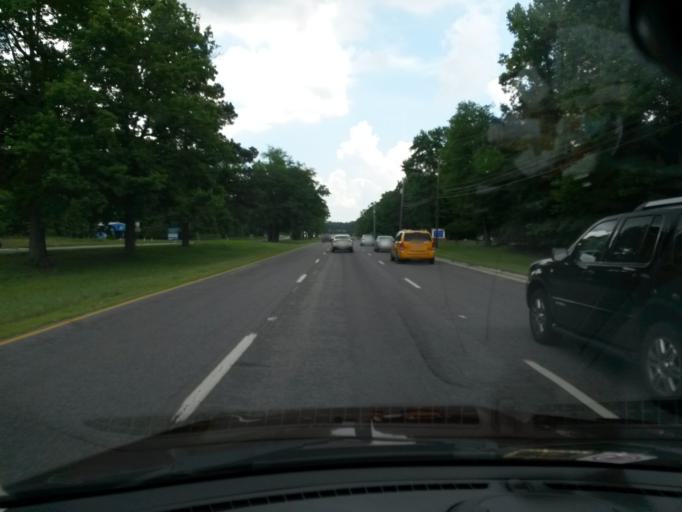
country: US
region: Virginia
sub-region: Chesterfield County
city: Enon
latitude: 37.3470
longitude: -77.3484
